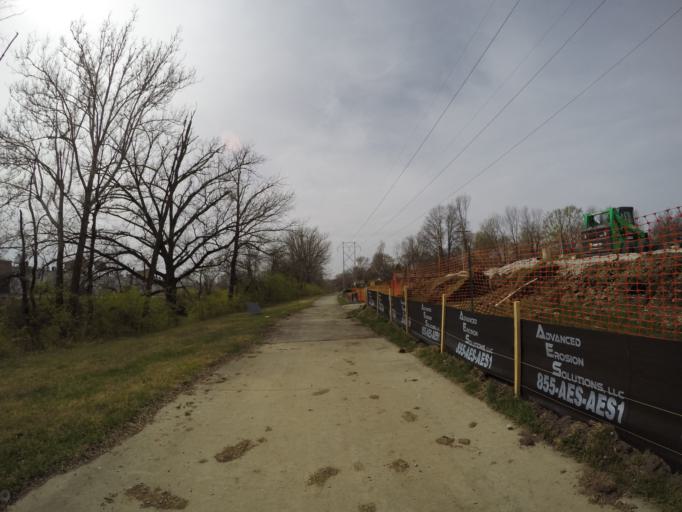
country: US
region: Kansas
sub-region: Johnson County
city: Leawood
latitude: 38.9425
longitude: -94.5971
